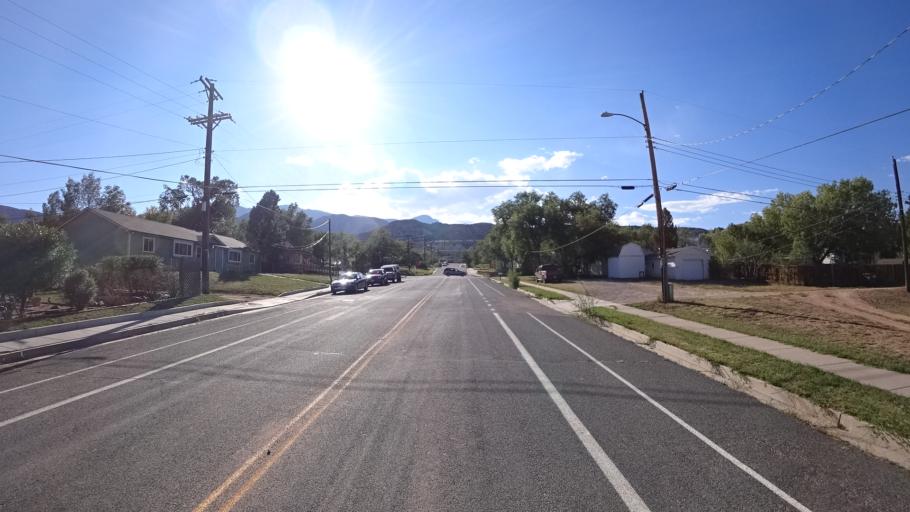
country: US
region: Colorado
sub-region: El Paso County
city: Colorado Springs
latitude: 38.8374
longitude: -104.8707
